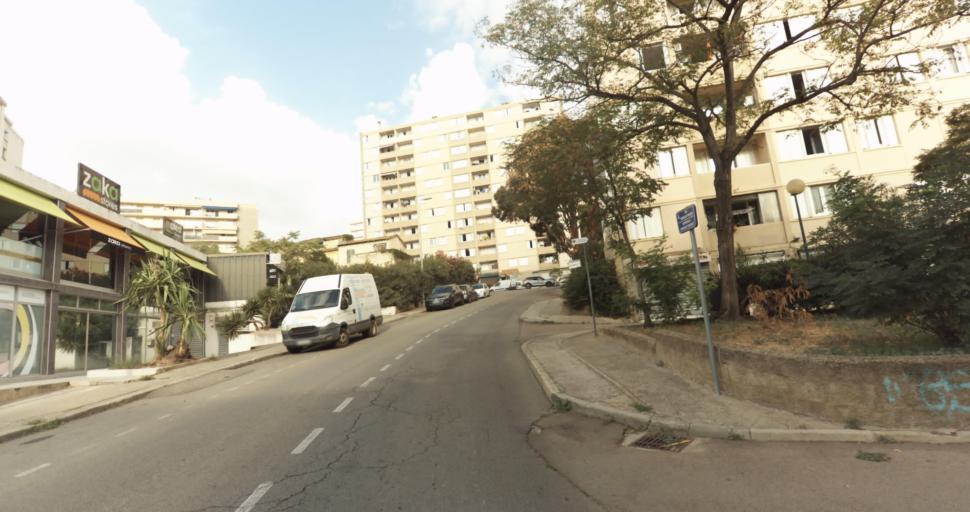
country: FR
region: Corsica
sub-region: Departement de la Corse-du-Sud
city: Ajaccio
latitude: 41.9311
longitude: 8.7345
